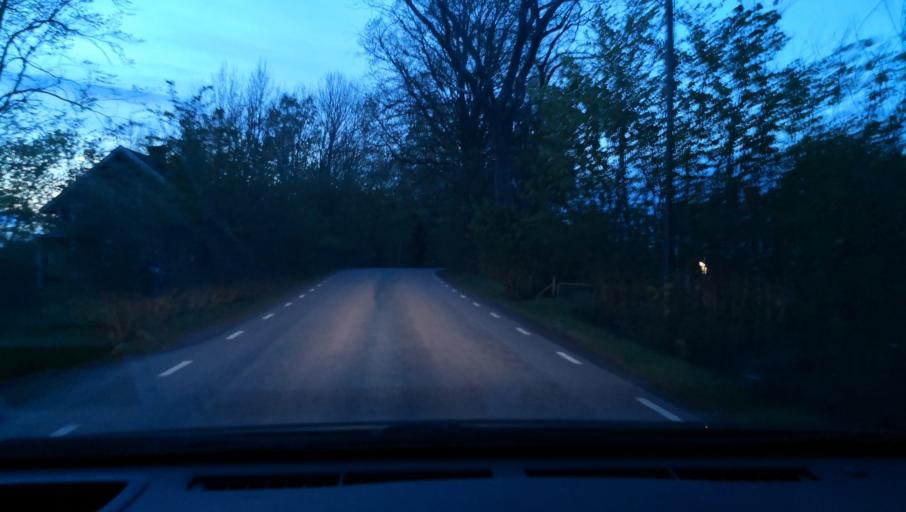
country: SE
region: OErebro
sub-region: Askersunds Kommun
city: Asbro
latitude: 59.0829
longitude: 15.0058
